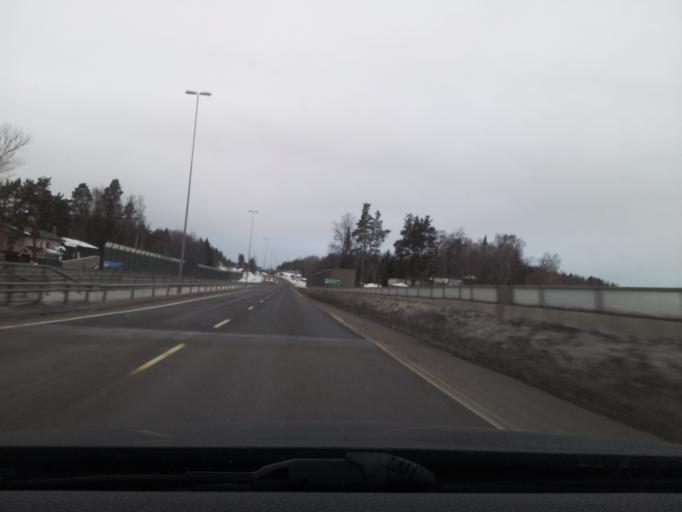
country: FI
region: Uusimaa
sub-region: Helsinki
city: Espoo
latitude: 60.1570
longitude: 24.6097
